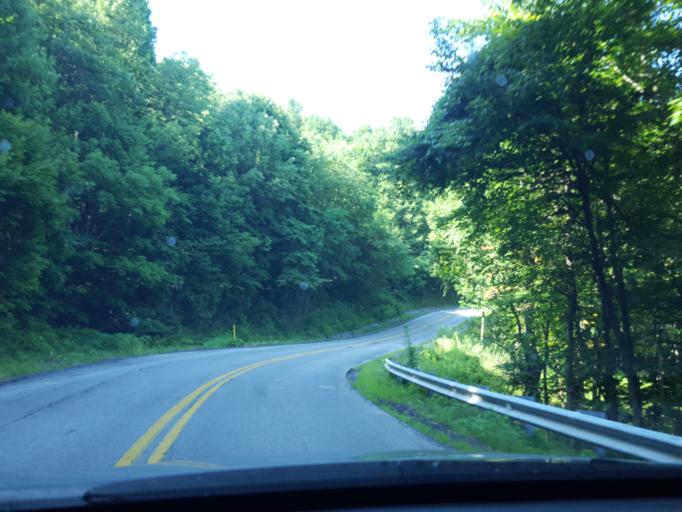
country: US
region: Virginia
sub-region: Nelson County
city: Nellysford
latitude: 37.9056
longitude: -78.9886
